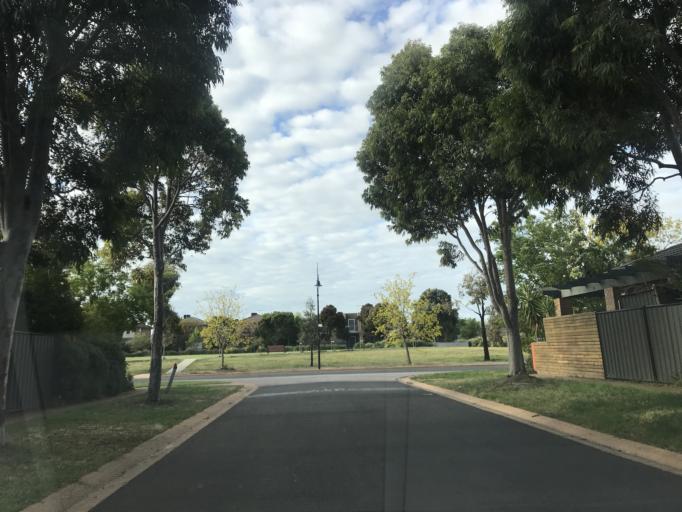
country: AU
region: Victoria
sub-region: Wyndham
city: Point Cook
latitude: -37.8945
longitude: 144.7330
